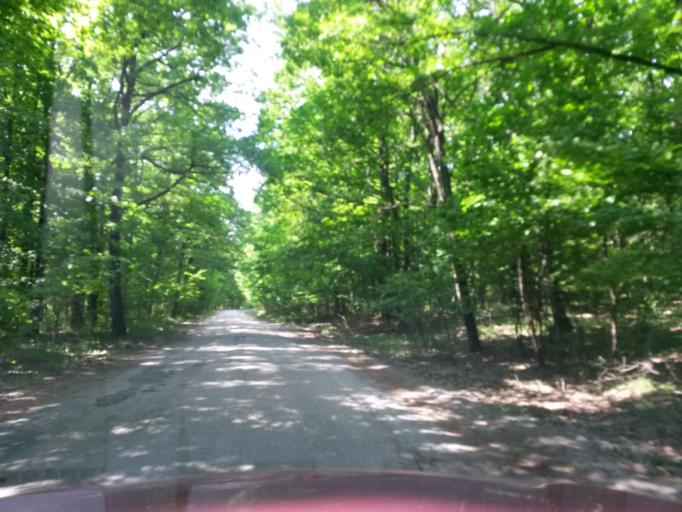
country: SK
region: Kosicky
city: Moldava nad Bodvou
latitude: 48.7134
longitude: 21.0251
